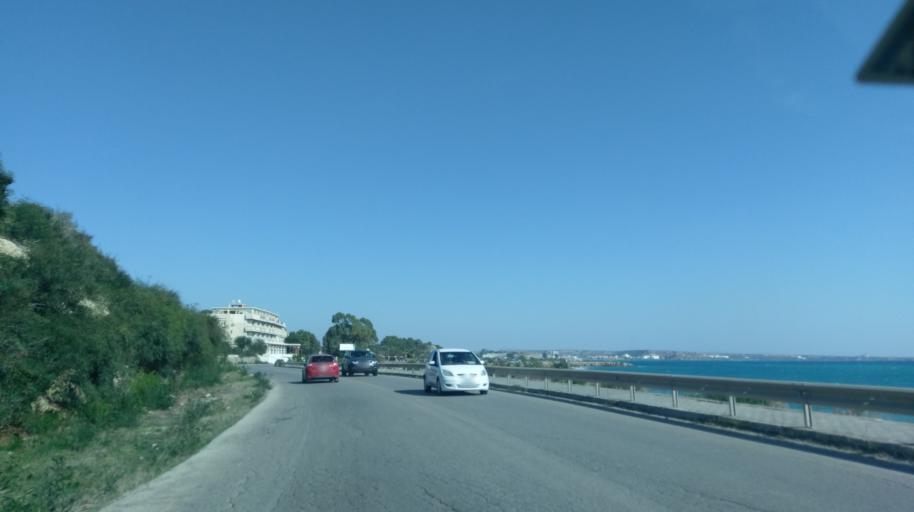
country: CY
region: Ammochostos
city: Trikomo
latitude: 35.3099
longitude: 33.9495
